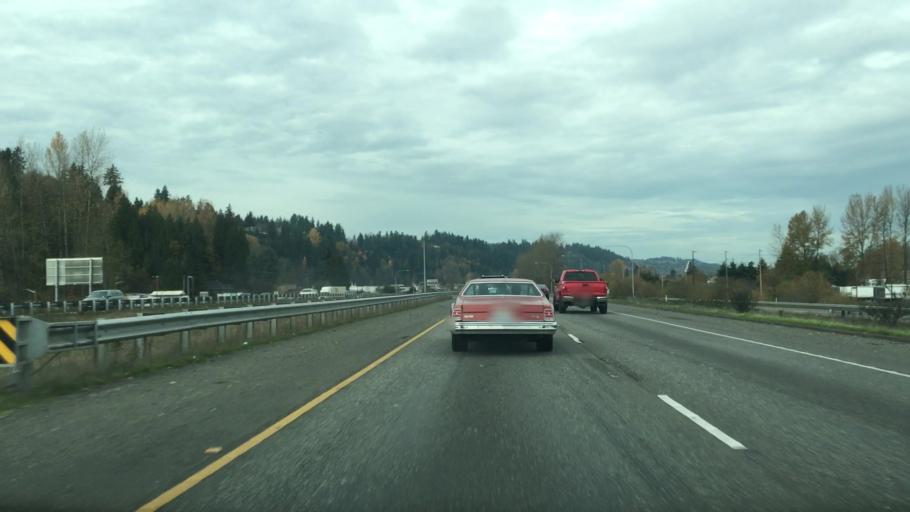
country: US
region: Washington
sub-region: King County
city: Pacific
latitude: 47.2509
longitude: -122.2574
